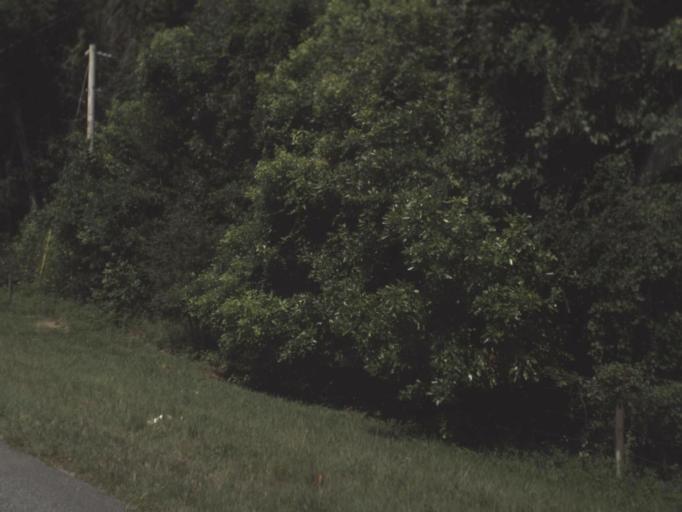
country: US
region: Florida
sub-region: Hernando County
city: North Brooksville
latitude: 28.6442
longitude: -82.3344
